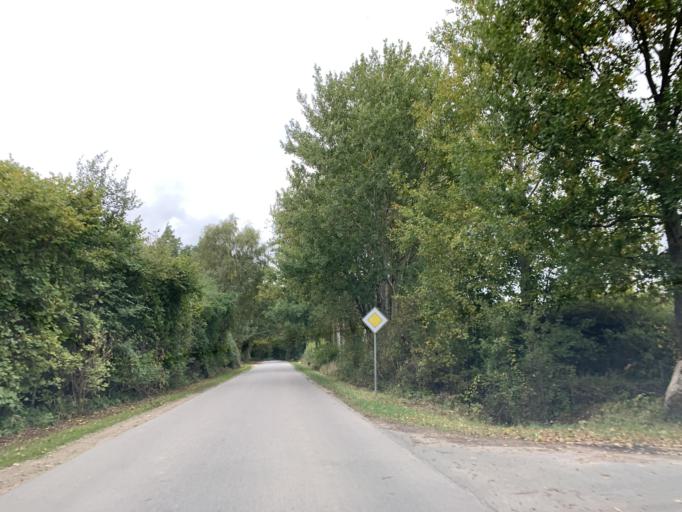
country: DE
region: Mecklenburg-Vorpommern
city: Blankensee
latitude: 53.4294
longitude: 13.2638
